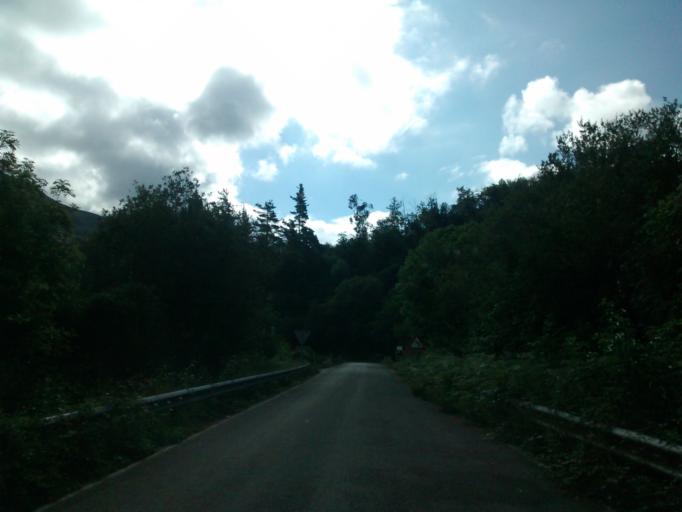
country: ES
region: Cantabria
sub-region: Provincia de Cantabria
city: Ruente
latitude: 43.2002
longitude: -4.3024
